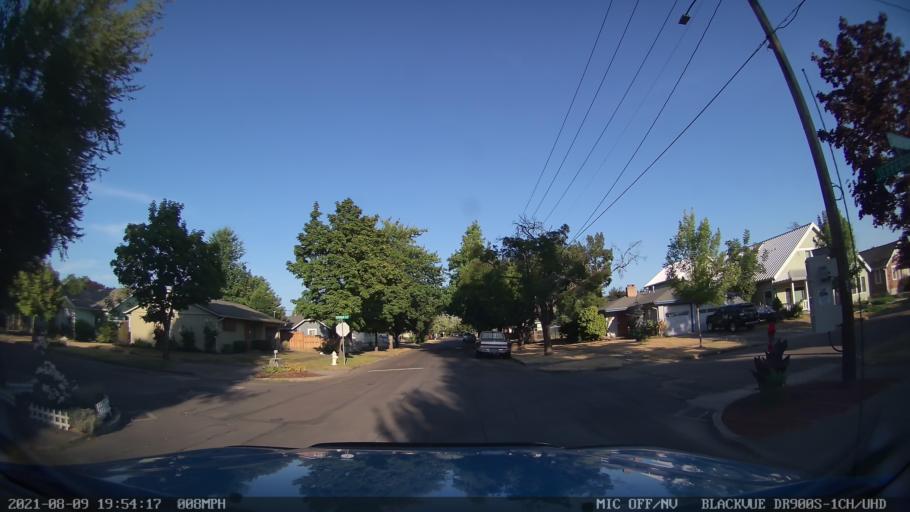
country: US
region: Oregon
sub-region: Marion County
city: Salem
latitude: 44.9549
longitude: -123.0273
